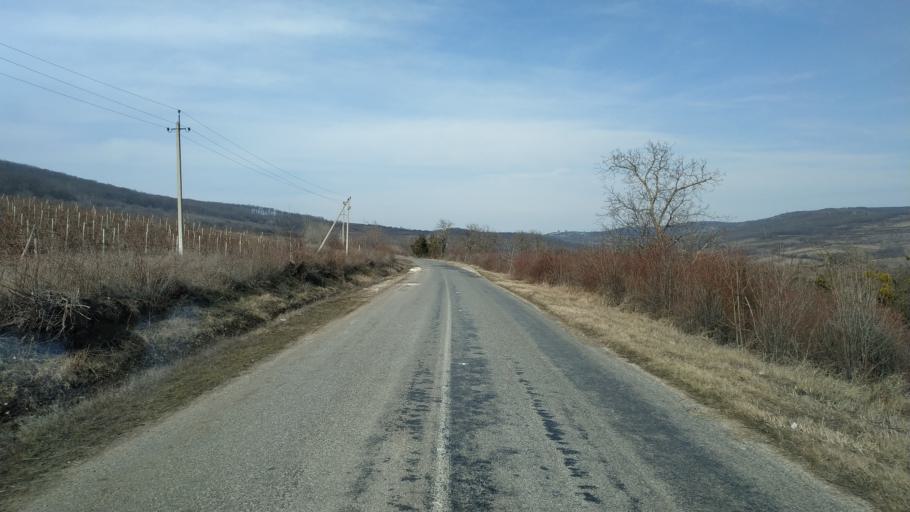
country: MD
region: Nisporeni
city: Nisporeni
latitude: 47.1762
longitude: 28.0855
